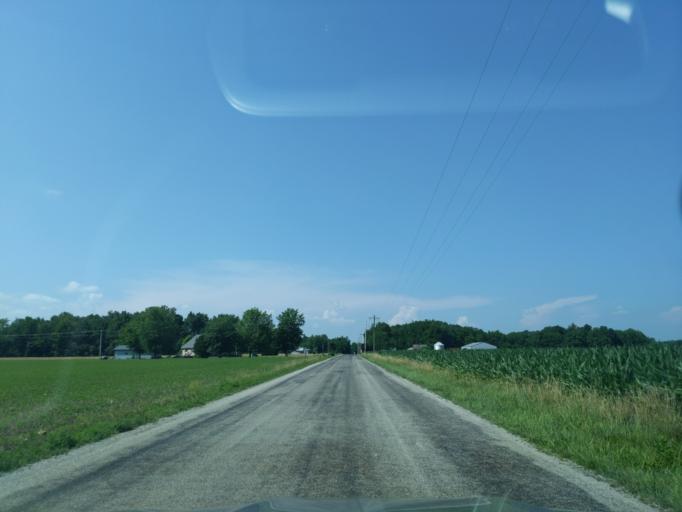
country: US
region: Indiana
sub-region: Ripley County
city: Osgood
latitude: 39.1459
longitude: -85.3388
